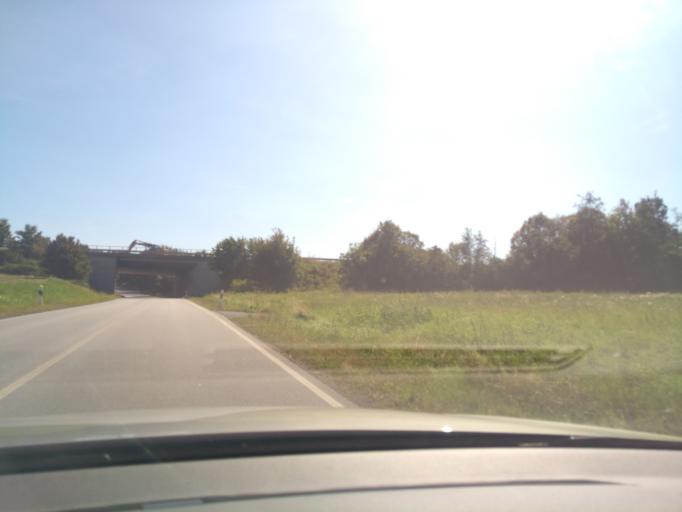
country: DE
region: Saxony
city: Goda
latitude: 51.2043
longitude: 14.3099
